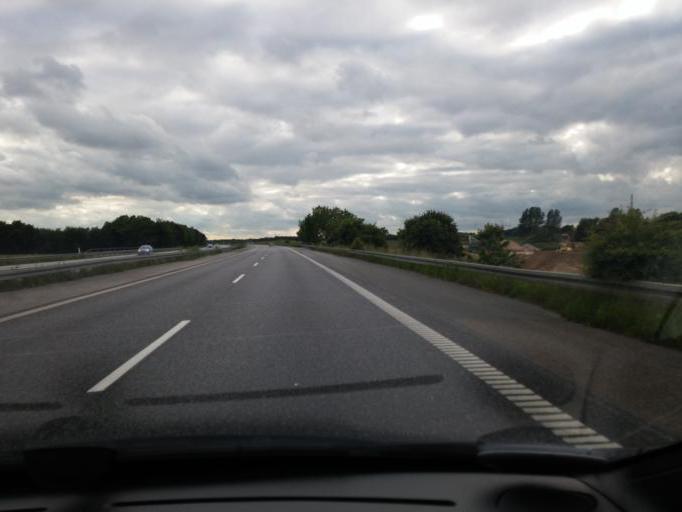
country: DK
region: Zealand
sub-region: Koge Kommune
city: Ejby
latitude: 55.4792
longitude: 12.1024
